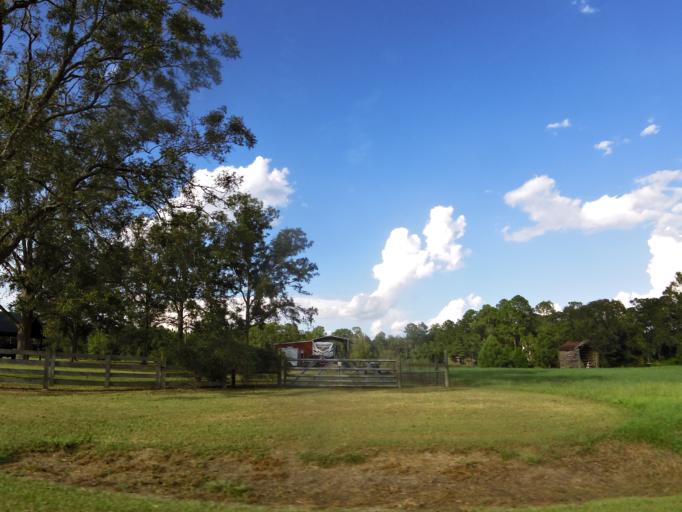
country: US
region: Georgia
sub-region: Brooks County
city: Quitman
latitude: 30.7864
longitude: -83.6339
